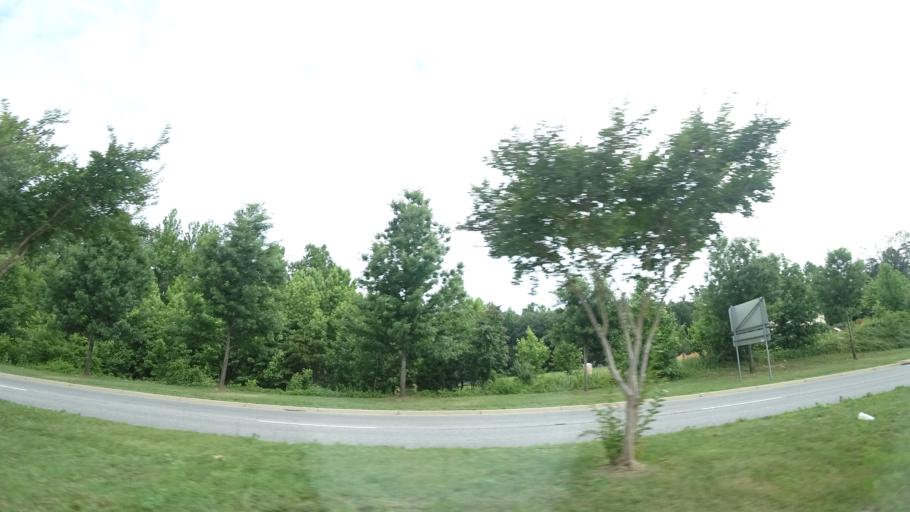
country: US
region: Virginia
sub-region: Spotsylvania County
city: Spotsylvania
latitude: 38.2062
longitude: -77.5937
